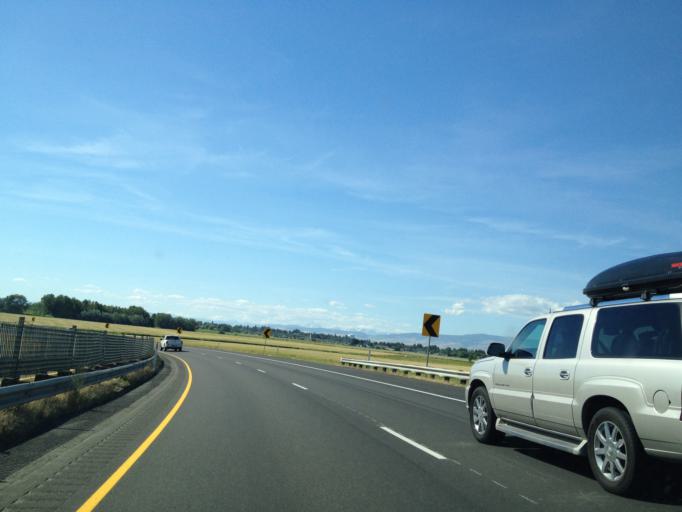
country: US
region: Washington
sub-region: Kittitas County
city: Ellensburg
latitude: 46.9715
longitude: -120.5117
